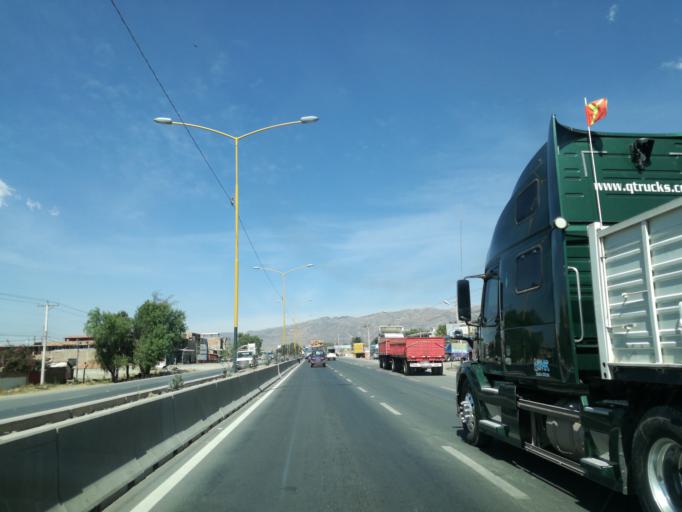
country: BO
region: Cochabamba
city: Sipe Sipe
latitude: -17.4095
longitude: -66.3322
